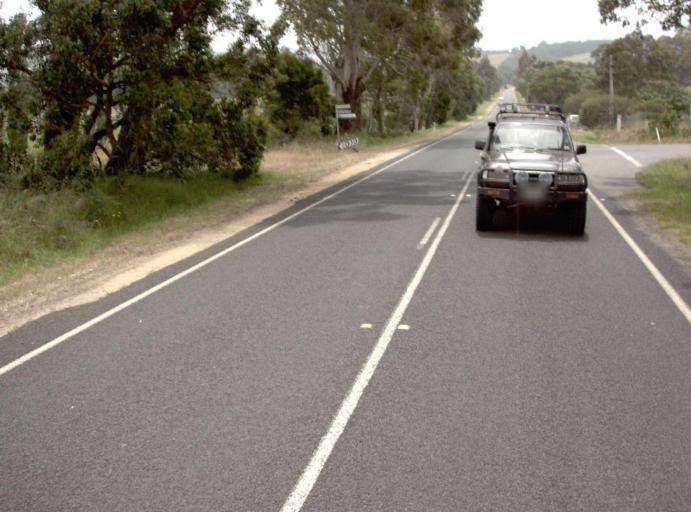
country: AU
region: Victoria
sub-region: Latrobe
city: Traralgon
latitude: -38.4736
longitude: 146.7169
